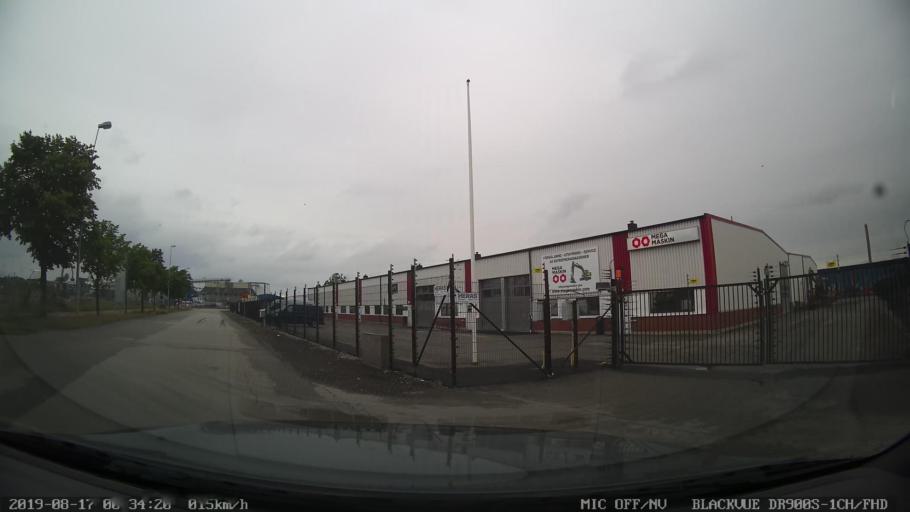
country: SE
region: Skane
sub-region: Landskrona
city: Landskrona
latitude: 55.8593
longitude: 12.8390
